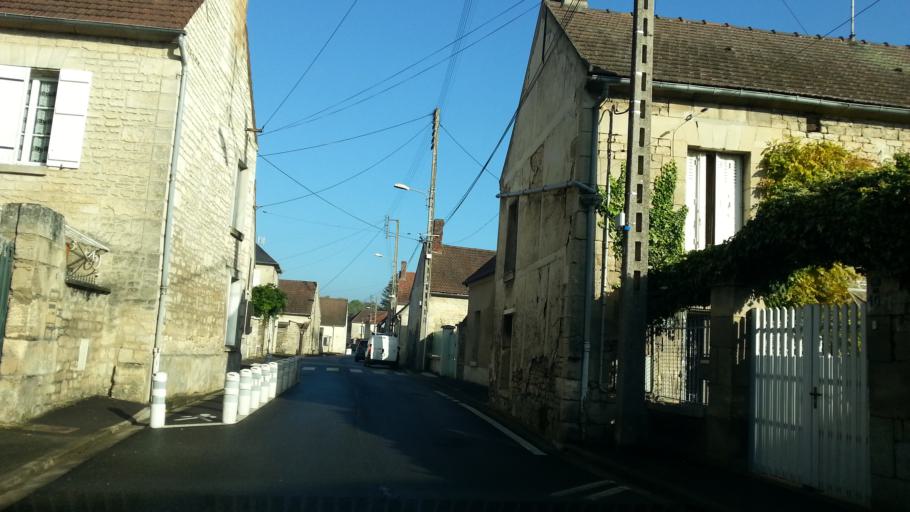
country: FR
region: Picardie
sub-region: Departement de l'Oise
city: Cires-les-Mello
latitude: 49.2758
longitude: 2.3573
